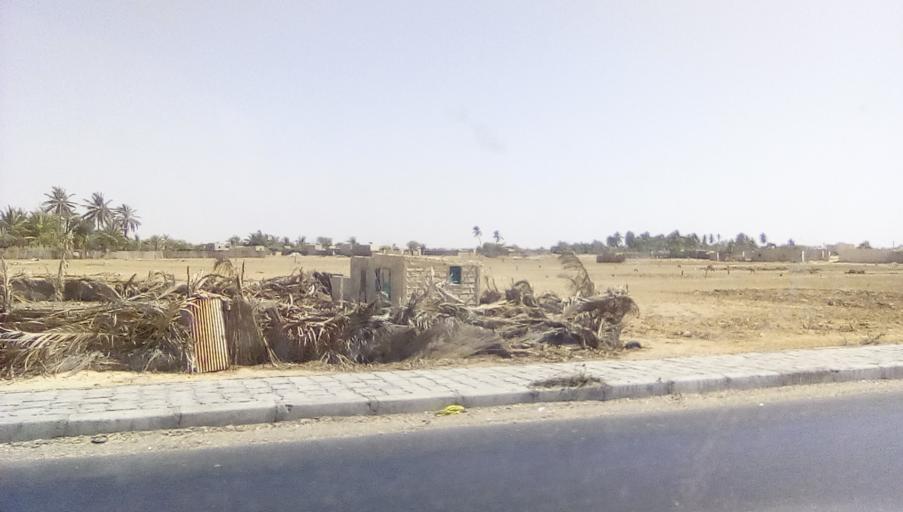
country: SN
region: Saint-Louis
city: Saint-Louis
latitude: 16.0375
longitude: -16.4649
